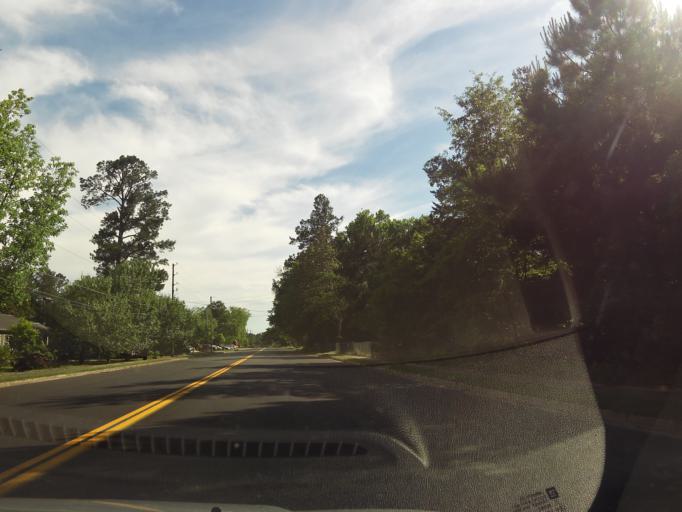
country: US
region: South Carolina
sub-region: Allendale County
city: Fairfax
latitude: 32.9704
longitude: -81.2331
